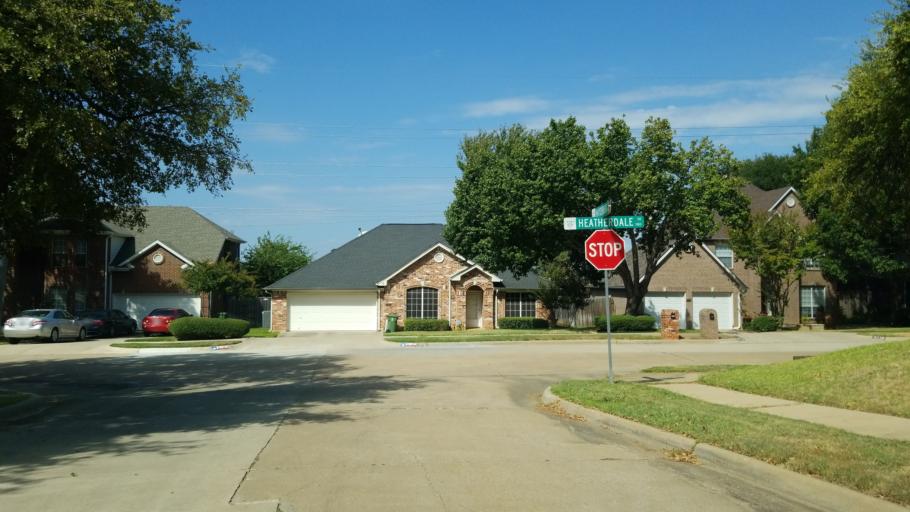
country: US
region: Texas
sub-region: Tarrant County
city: Grapevine
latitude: 32.8865
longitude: -97.0945
